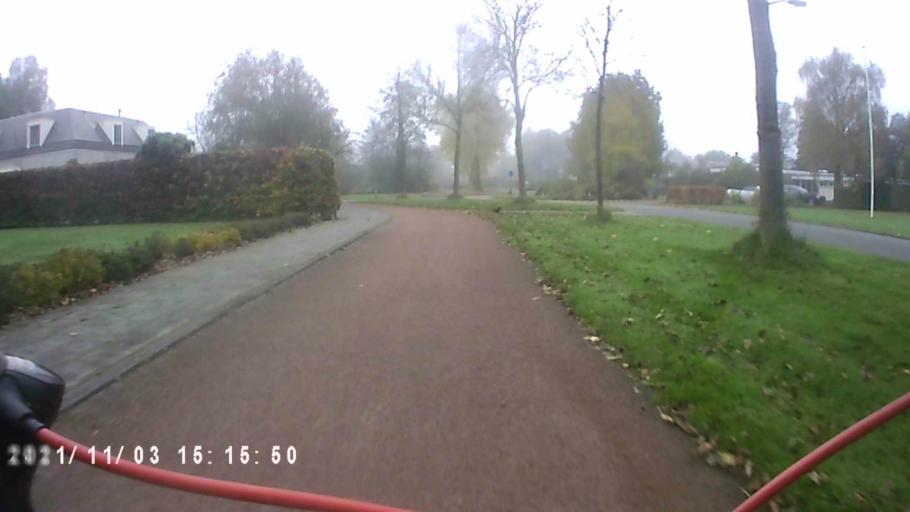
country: NL
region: Groningen
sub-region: Gemeente Leek
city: Leek
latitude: 53.1674
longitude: 6.3613
